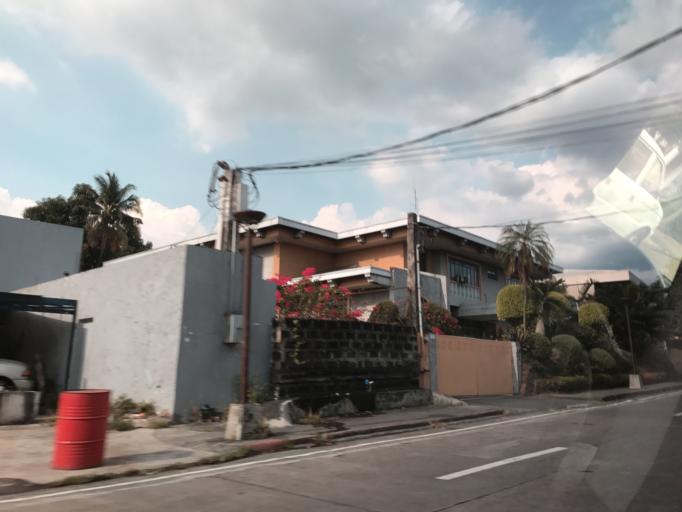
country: PH
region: Metro Manila
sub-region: Pasig
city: Pasig City
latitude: 14.6008
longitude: 121.0565
